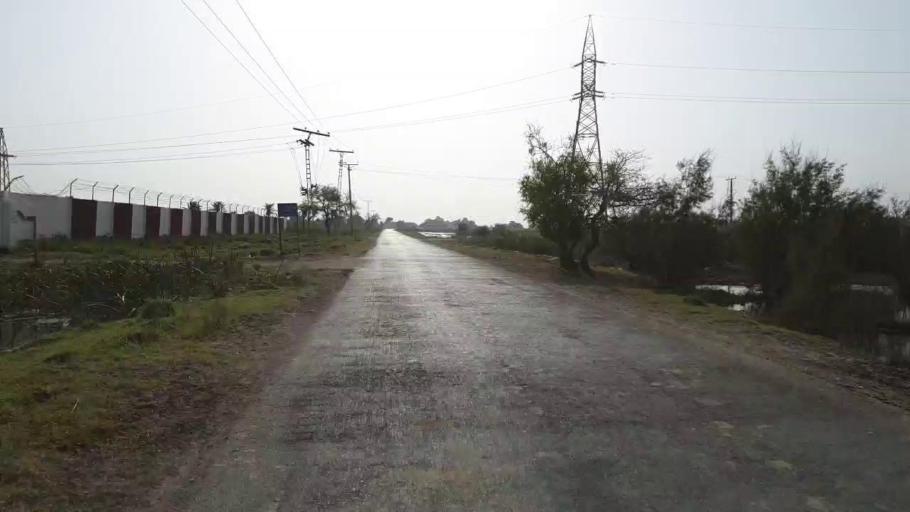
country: PK
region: Sindh
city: Jam Sahib
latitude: 26.3791
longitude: 68.8948
